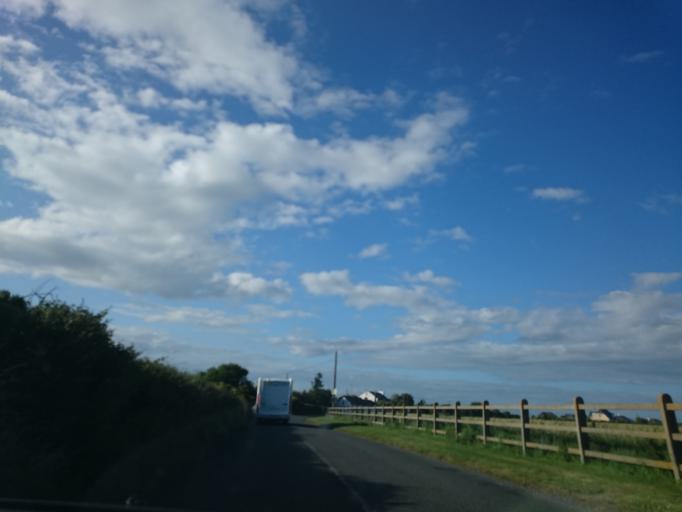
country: IE
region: Leinster
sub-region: Loch Garman
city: Loch Garman
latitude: 52.1814
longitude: -6.5819
